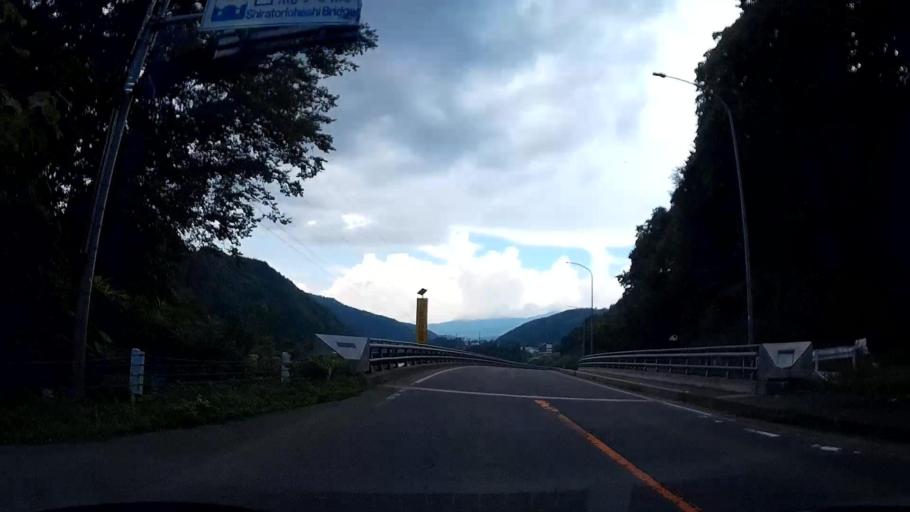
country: JP
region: Nagano
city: Iiyama
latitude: 36.9851
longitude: 138.5200
